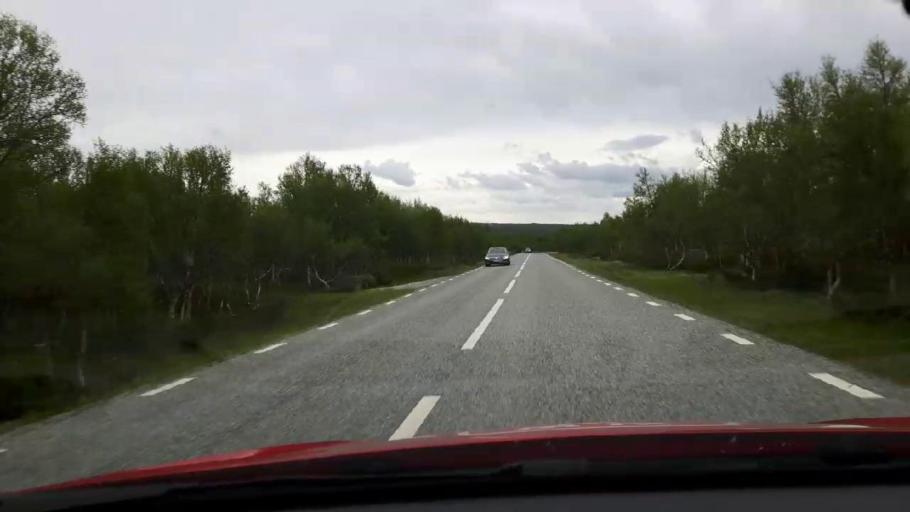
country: NO
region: Sor-Trondelag
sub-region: Tydal
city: Aas
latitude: 62.6372
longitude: 12.1055
